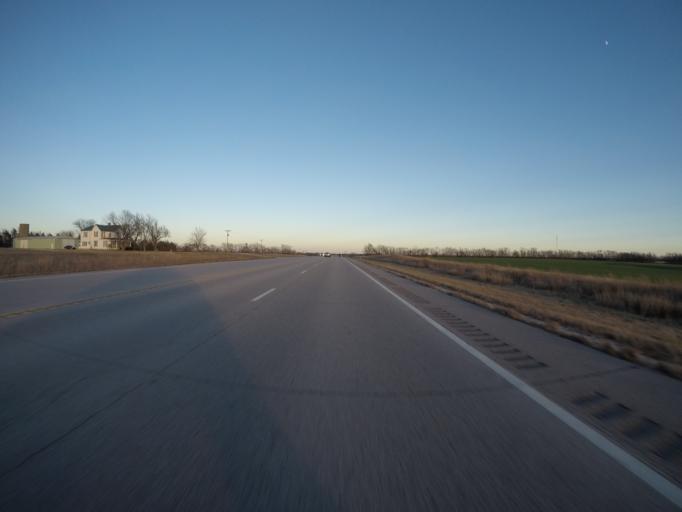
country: US
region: Kansas
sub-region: Marion County
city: Peabody
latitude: 38.1746
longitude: -97.1475
